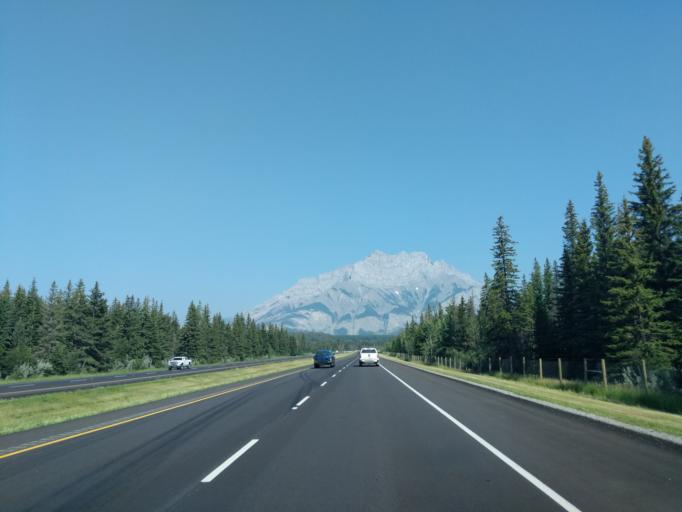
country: CA
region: Alberta
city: Banff
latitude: 51.1769
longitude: -115.4742
